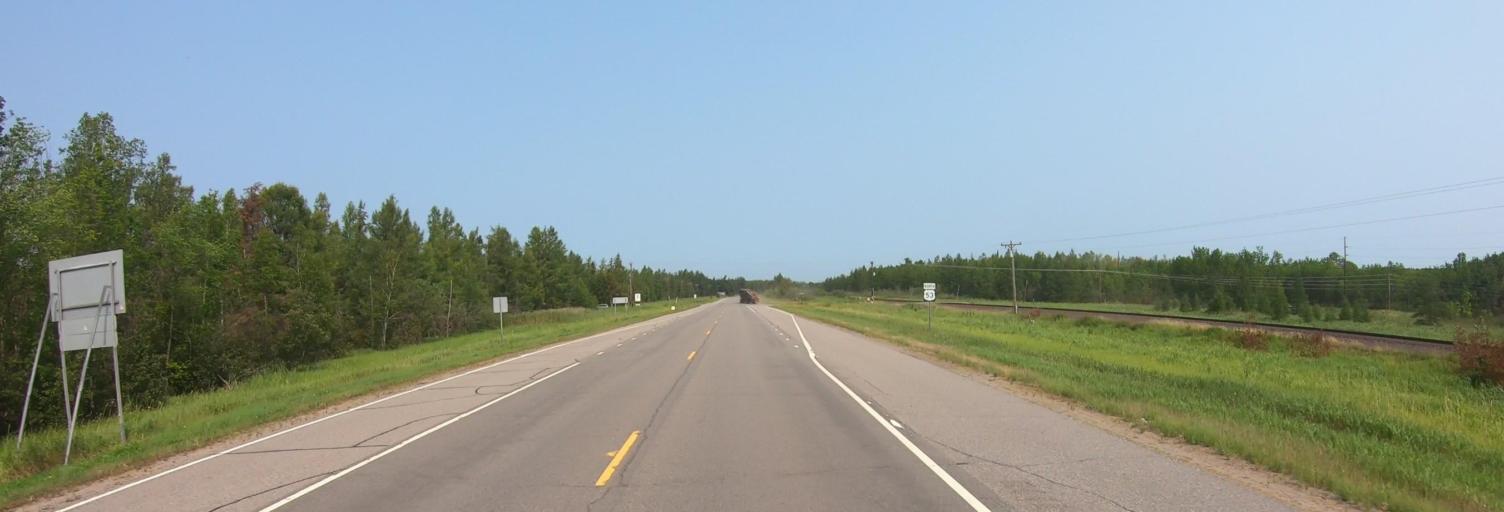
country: US
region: Minnesota
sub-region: Saint Louis County
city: Mountain Iron
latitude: 48.0349
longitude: -92.8317
